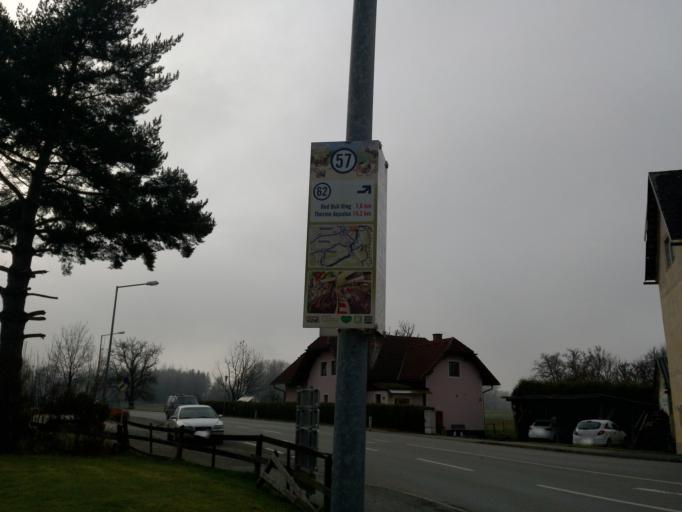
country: AT
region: Styria
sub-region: Politischer Bezirk Murtal
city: Apfelberg
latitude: 47.2028
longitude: 14.8351
